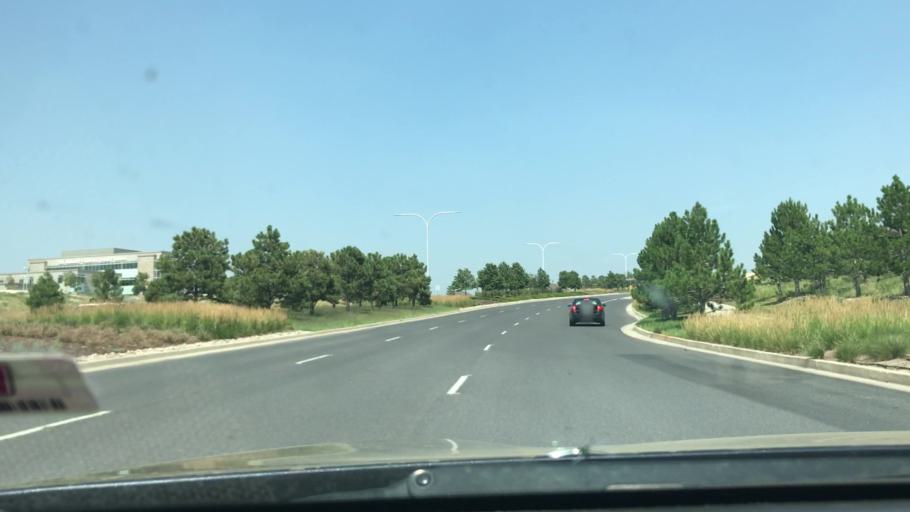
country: US
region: Colorado
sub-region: El Paso County
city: Black Forest
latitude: 38.9741
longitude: -104.7475
